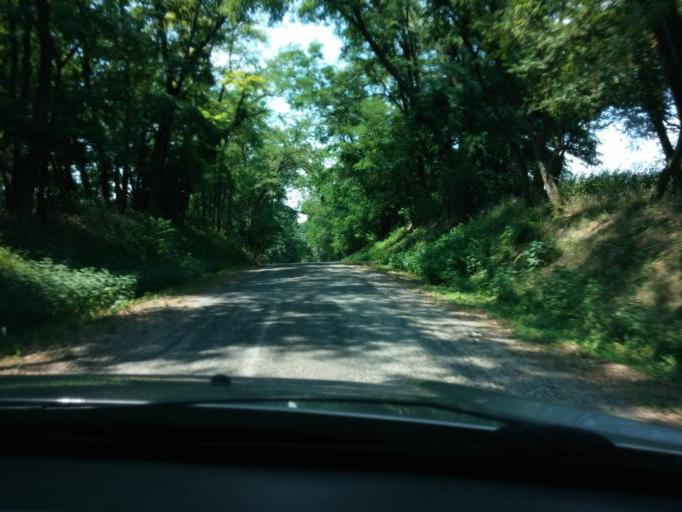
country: HU
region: Somogy
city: Kaposvar
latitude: 46.2552
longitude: 17.8182
